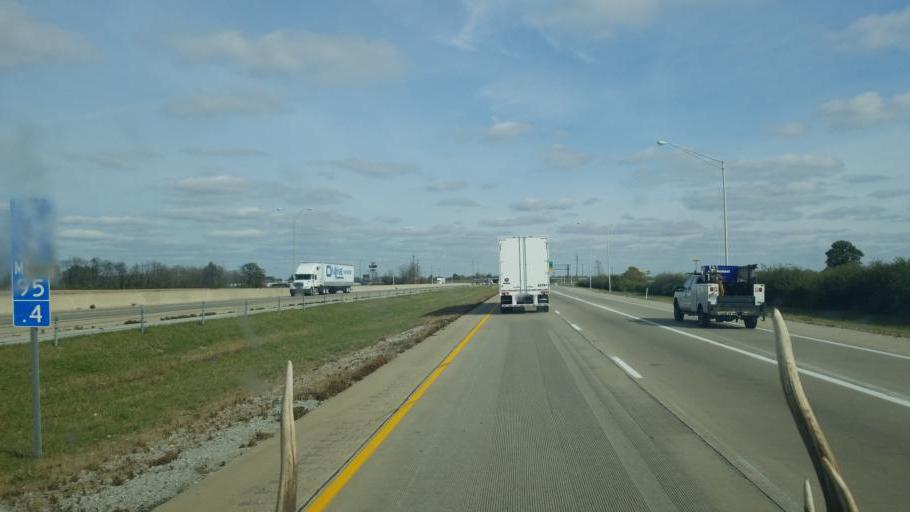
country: US
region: Indiana
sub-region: Marion County
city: Cumberland
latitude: 39.8163
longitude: -85.9253
